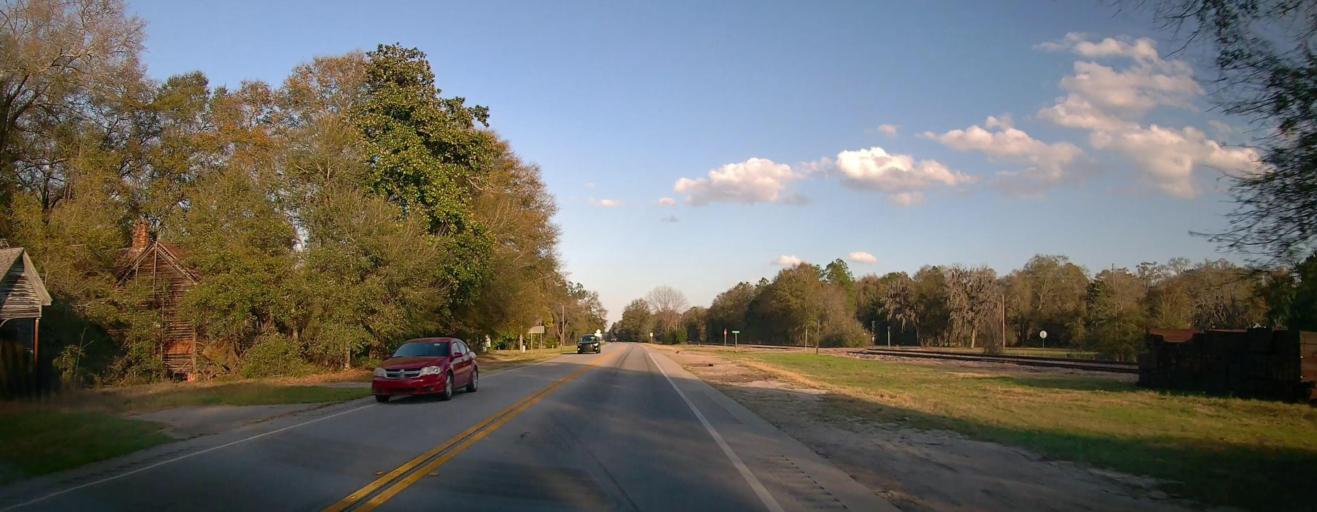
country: US
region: Georgia
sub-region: Bryan County
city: Pembroke
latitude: 32.1445
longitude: -81.7465
